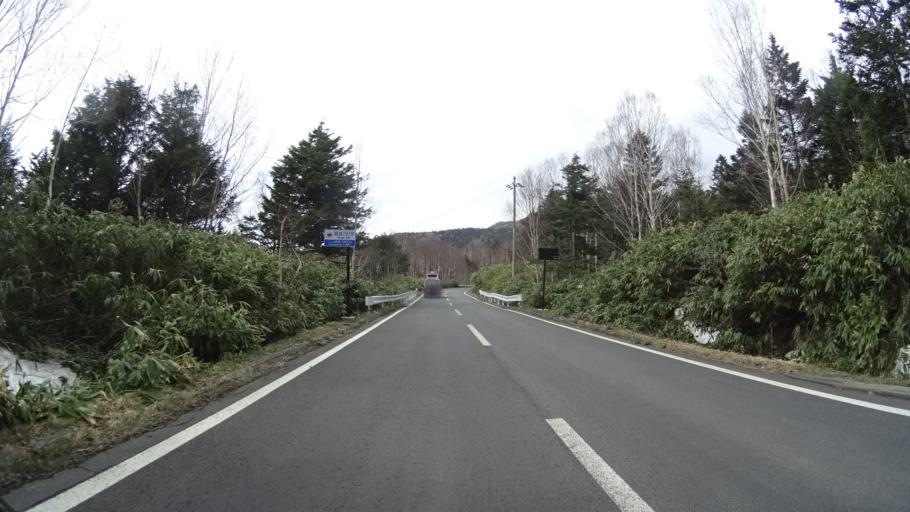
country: JP
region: Nagano
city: Nakano
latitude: 36.6771
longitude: 138.5074
